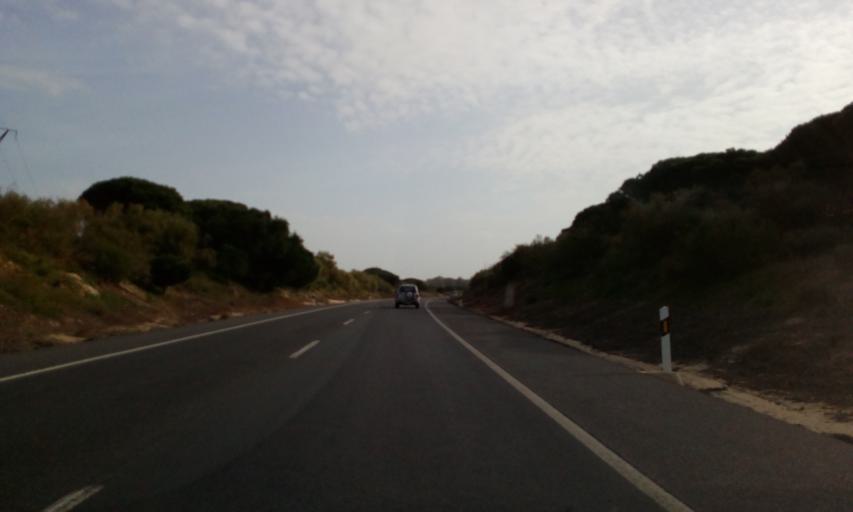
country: ES
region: Andalusia
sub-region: Provincia de Huelva
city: Palos de la Frontera
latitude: 37.1696
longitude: -6.8942
